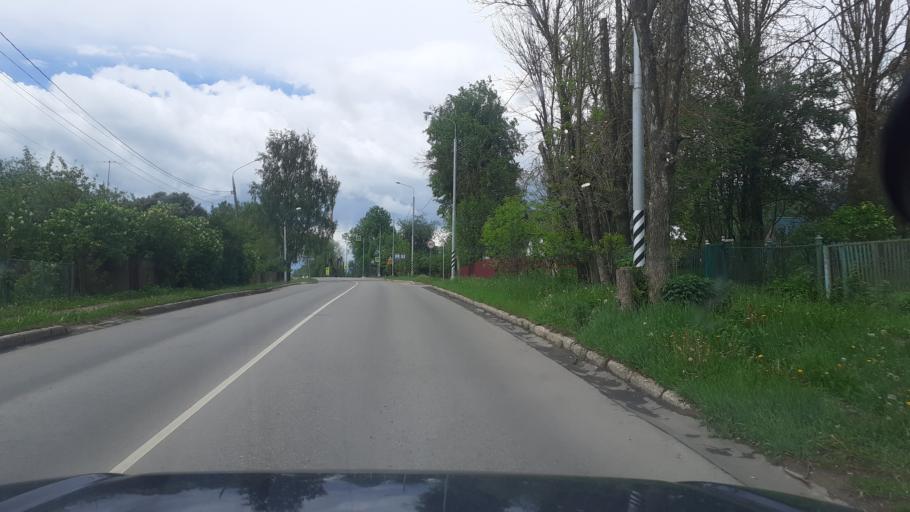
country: RU
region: Moskovskaya
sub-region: Volokolamskiy Rayon
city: Volokolamsk
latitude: 56.0431
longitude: 35.9536
